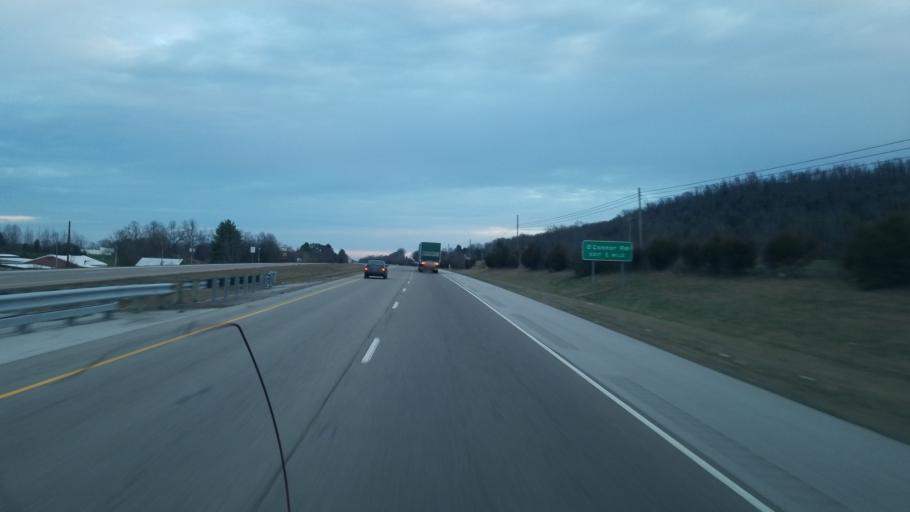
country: US
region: Tennessee
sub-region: White County
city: Sparta
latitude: 35.9988
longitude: -85.5030
